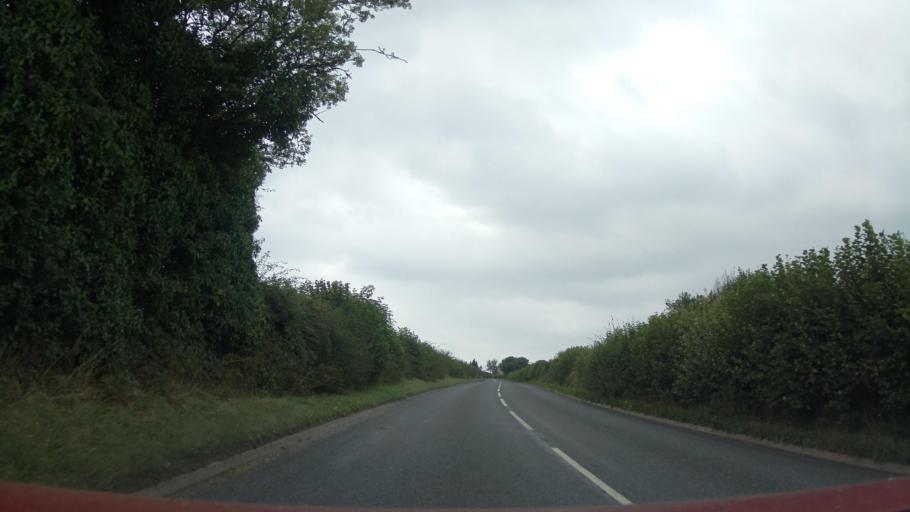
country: GB
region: England
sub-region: Staffordshire
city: Cheadle
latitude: 53.0197
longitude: -2.0034
